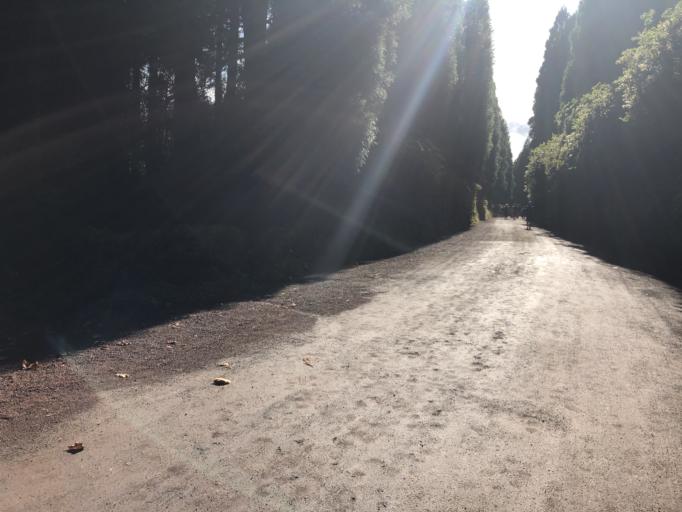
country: PT
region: Azores
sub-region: Ponta Delgada
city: Arrifes
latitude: 37.8399
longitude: -25.7602
